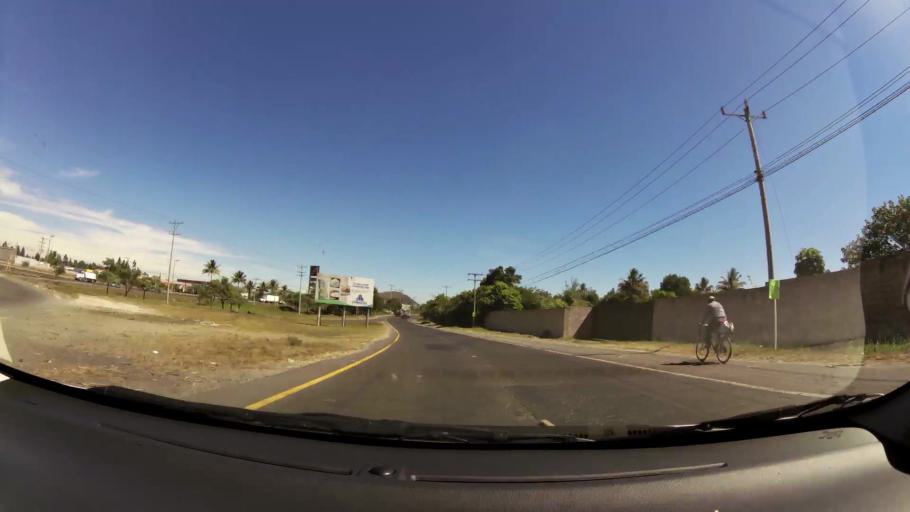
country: SV
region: La Libertad
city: San Juan Opico
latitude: 13.7868
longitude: -89.3591
